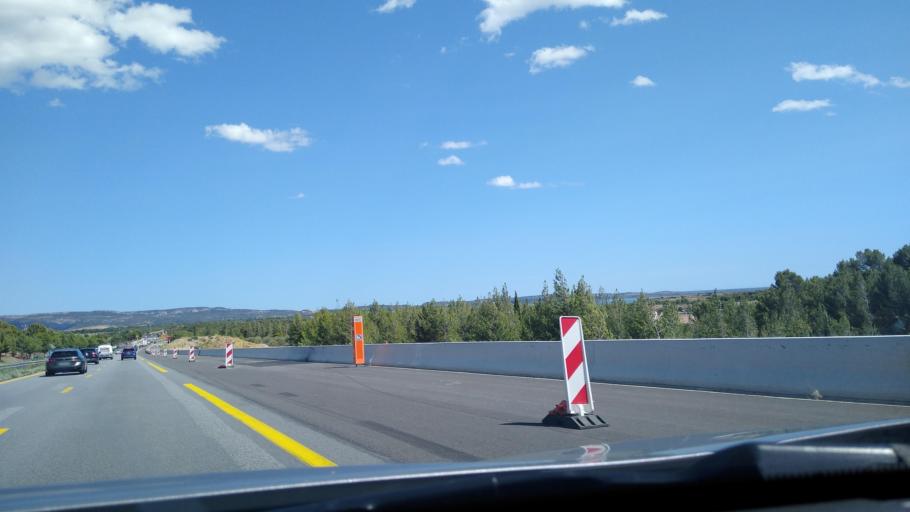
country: FR
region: Languedoc-Roussillon
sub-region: Departement de l'Aude
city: Narbonne
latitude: 43.1522
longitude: 2.9715
